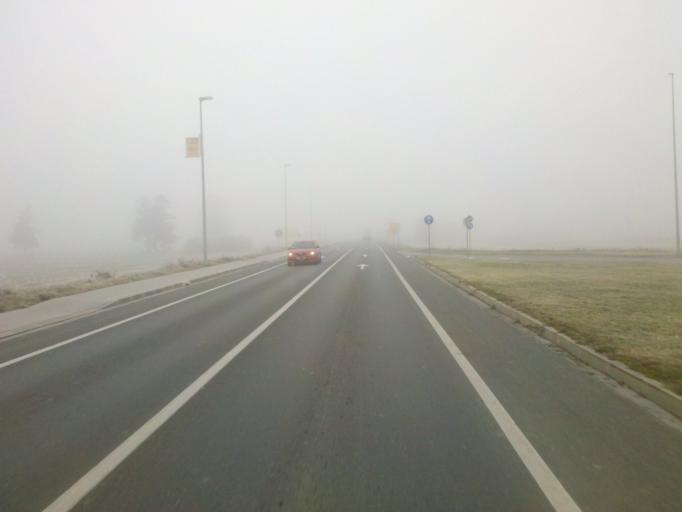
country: HR
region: Varazdinska
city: Sracinec
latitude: 46.3209
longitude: 16.3057
